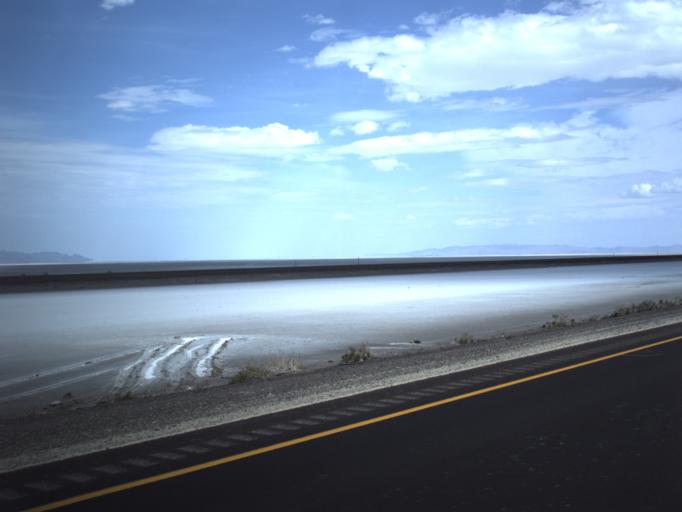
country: US
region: Utah
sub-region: Tooele County
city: Wendover
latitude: 40.7340
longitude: -113.6363
